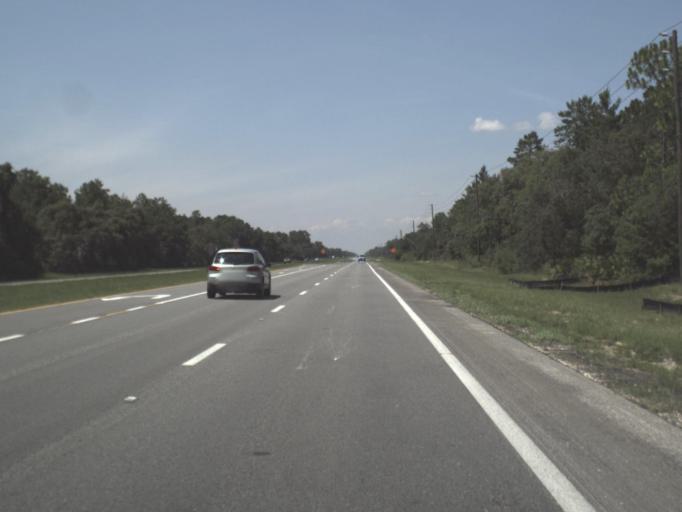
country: US
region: Florida
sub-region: Hernando County
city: North Weeki Wachee
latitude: 28.6100
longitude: -82.5517
